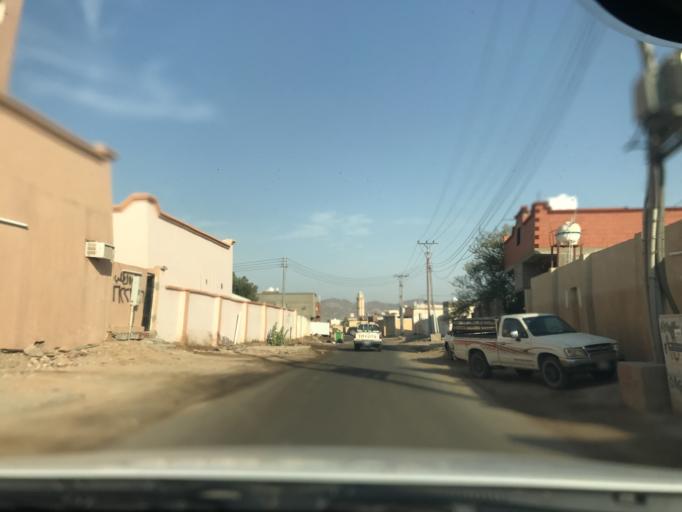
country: SA
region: Makkah
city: Al Jumum
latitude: 21.4417
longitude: 39.5204
